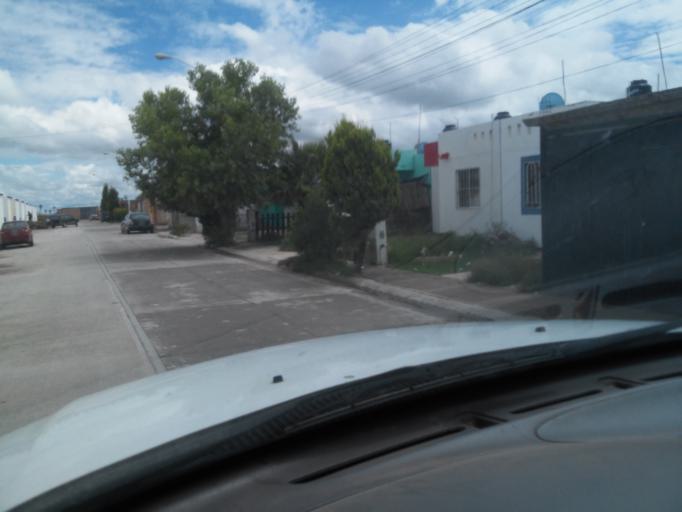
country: MX
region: Durango
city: Victoria de Durango
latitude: 24.0203
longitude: -104.6115
